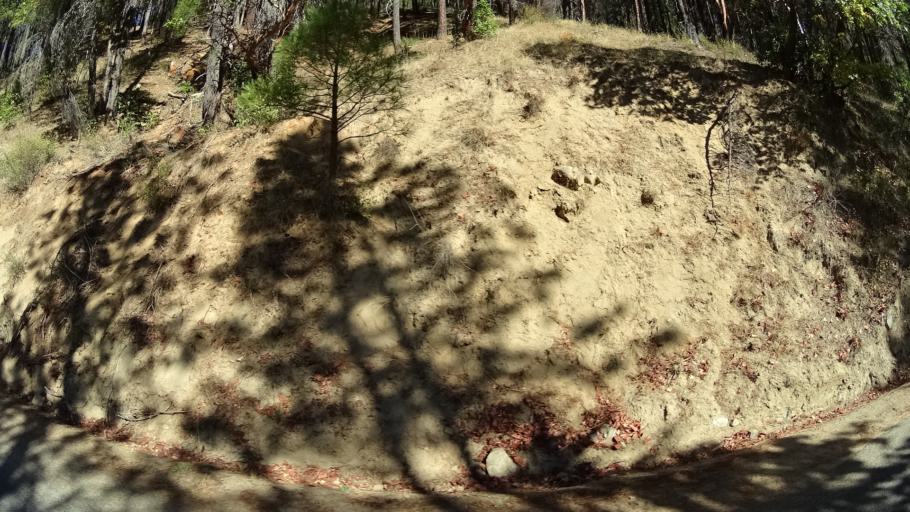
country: US
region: California
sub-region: Siskiyou County
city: Happy Camp
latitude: 41.3208
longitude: -123.1760
